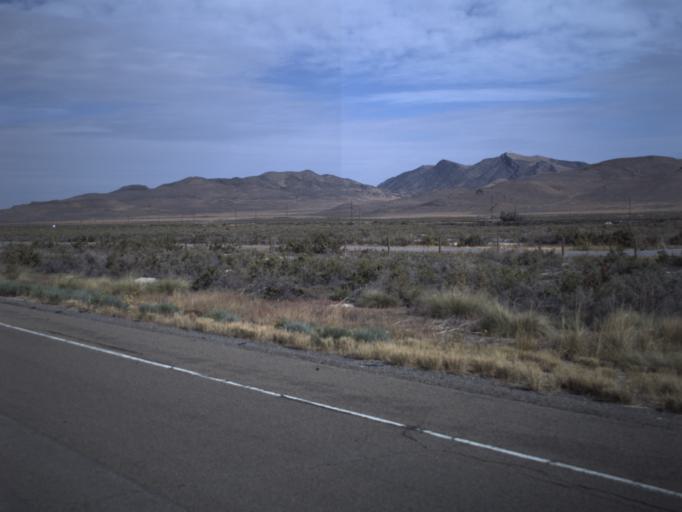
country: US
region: Utah
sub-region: Tooele County
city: Grantsville
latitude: 40.7668
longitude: -112.7882
